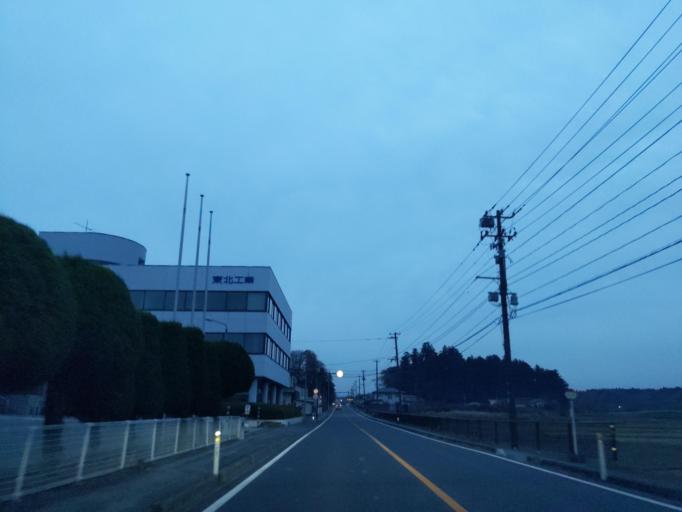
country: JP
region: Fukushima
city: Koriyama
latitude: 37.3428
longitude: 140.4047
